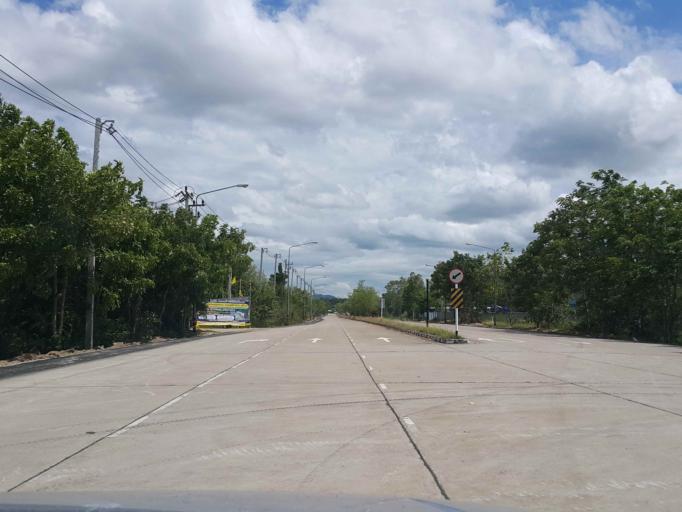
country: TH
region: Tak
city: Tak
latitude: 16.8612
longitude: 99.1147
